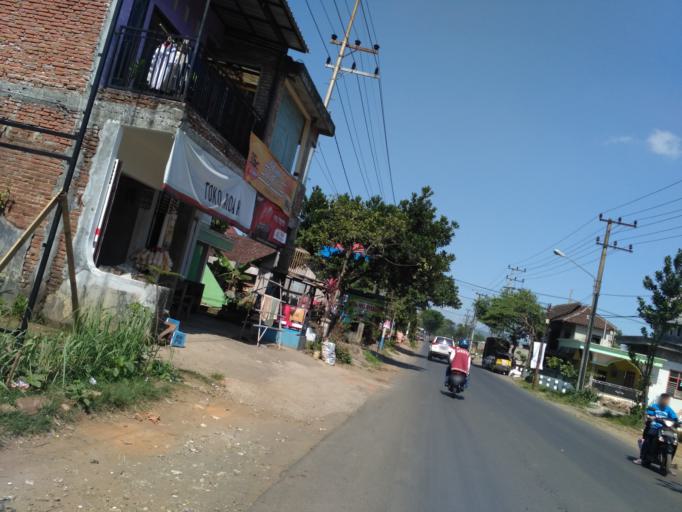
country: ID
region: East Java
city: Tamiajeng
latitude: -7.9542
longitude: 112.7007
